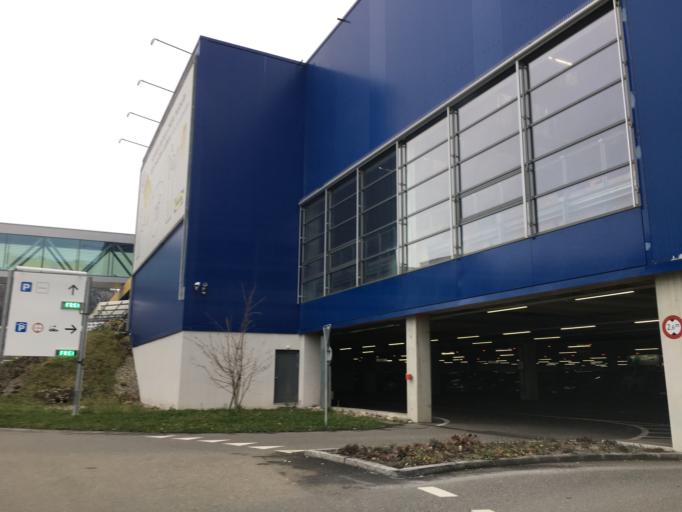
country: CH
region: Aargau
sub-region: Bezirk Baden
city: Spreitenbach
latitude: 47.4210
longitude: 8.3769
